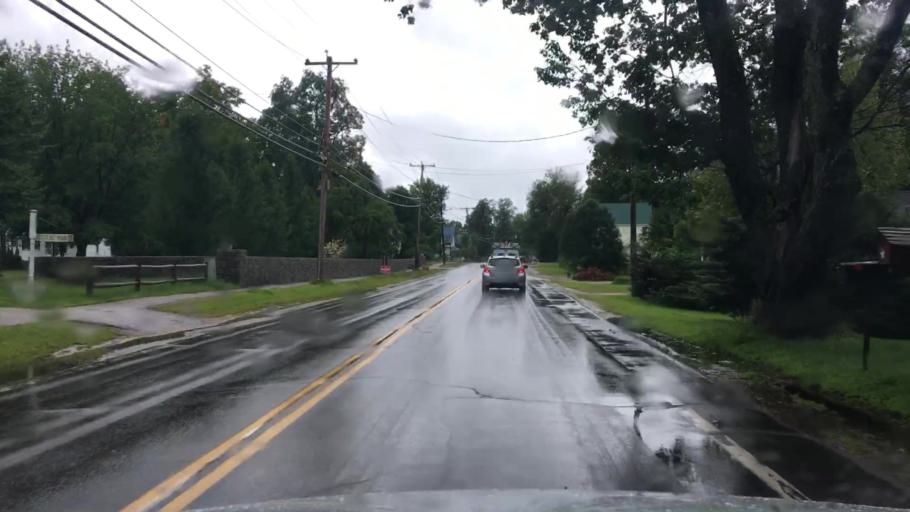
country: US
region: New Hampshire
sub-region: Carroll County
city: Conway
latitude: 43.9794
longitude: -71.1113
